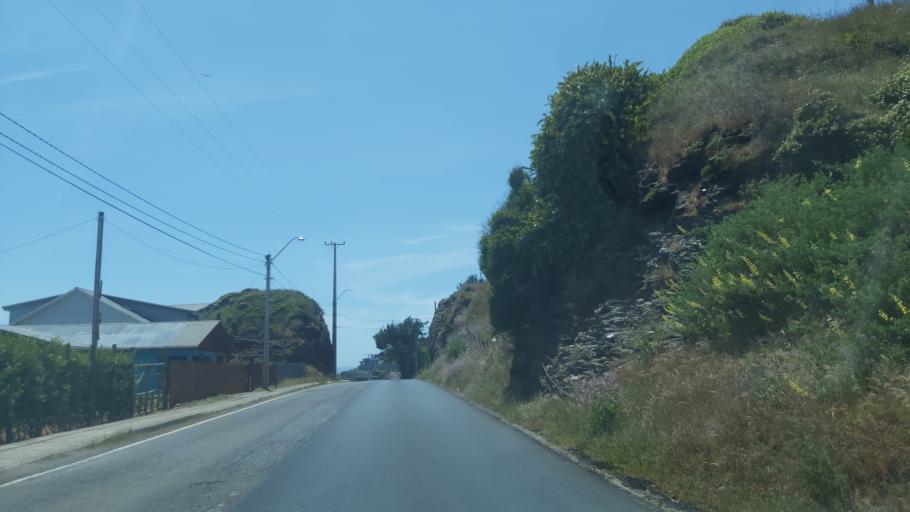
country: CL
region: Maule
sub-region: Provincia de Cauquenes
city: Cauquenes
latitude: -35.8390
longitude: -72.6270
